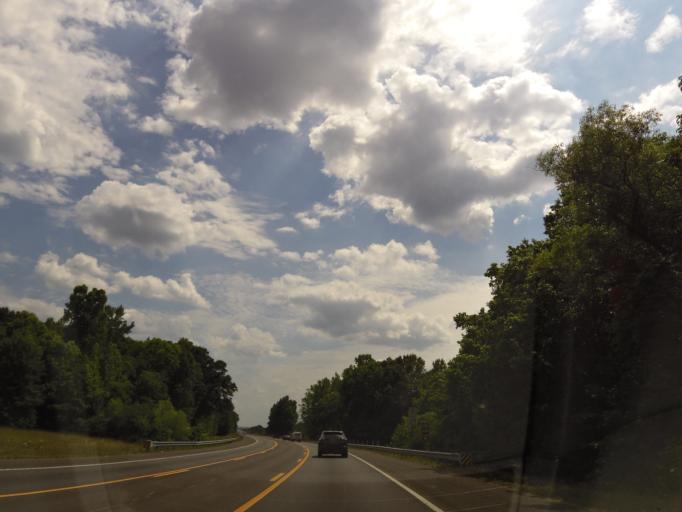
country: US
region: Tennessee
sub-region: Marion County
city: Whitwell
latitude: 35.1888
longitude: -85.5247
